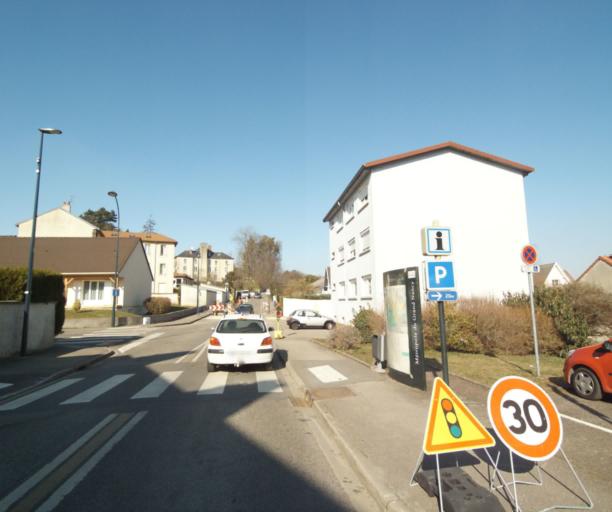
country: FR
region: Lorraine
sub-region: Departement de Meurthe-et-Moselle
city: Vandoeuvre-les-Nancy
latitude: 48.6472
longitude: 6.1756
